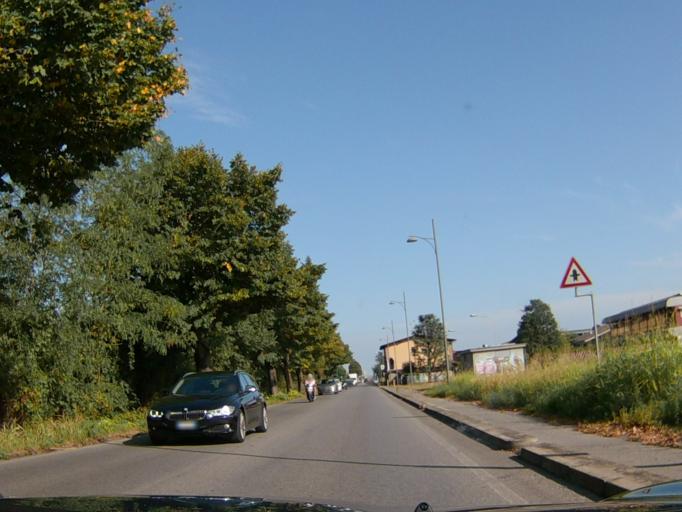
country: IT
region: Lombardy
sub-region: Provincia di Brescia
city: Cologne
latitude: 45.5776
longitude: 9.9385
